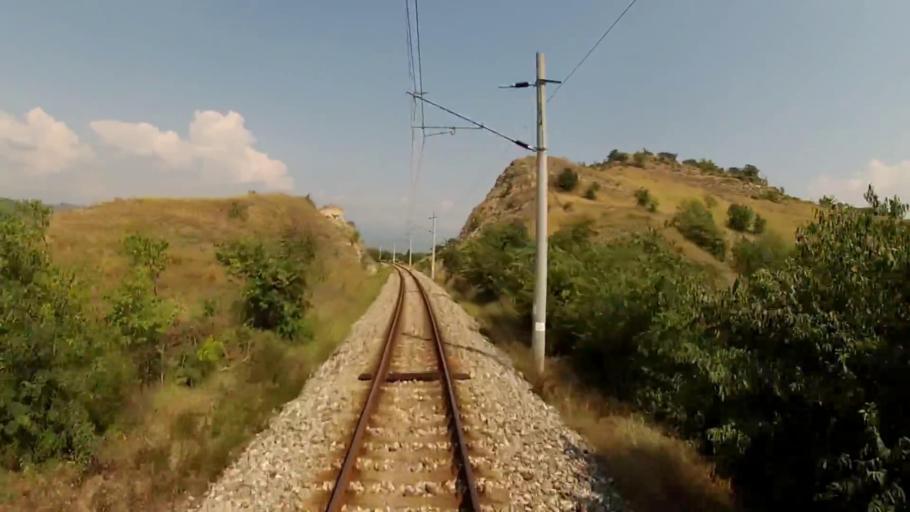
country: BG
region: Blagoevgrad
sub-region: Obshtina Strumyani
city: Strumyani
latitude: 41.5938
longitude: 23.2327
